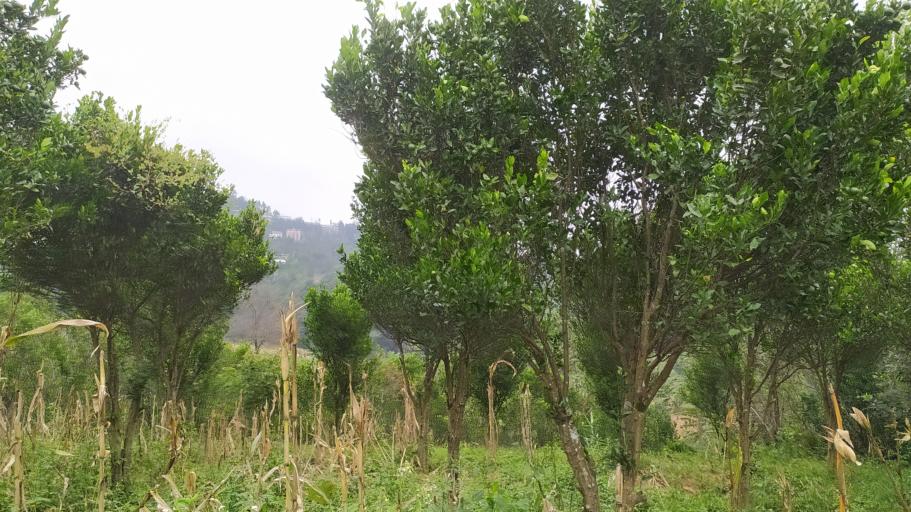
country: NP
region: Central Region
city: Panaoti
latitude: 27.5827
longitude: 85.5331
